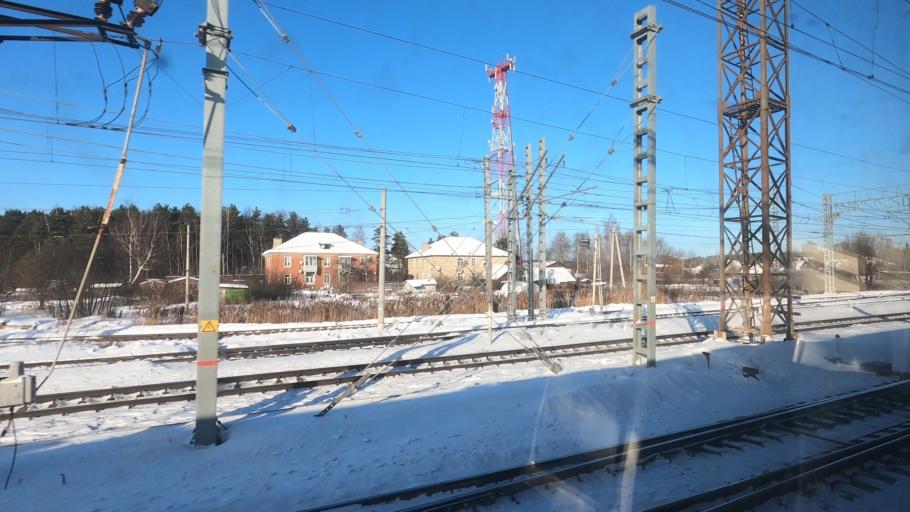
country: RU
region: Moskovskaya
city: Fryazevo
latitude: 55.7308
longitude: 38.4586
